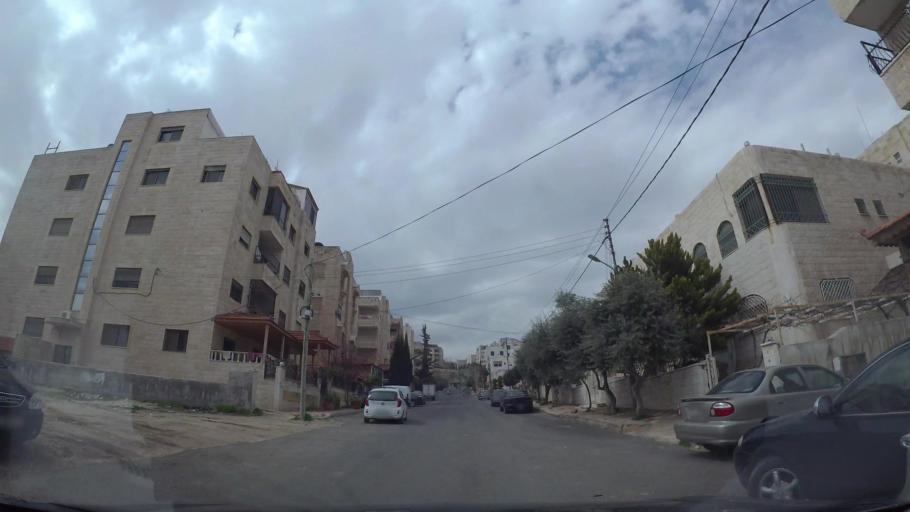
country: JO
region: Amman
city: Amman
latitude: 31.9910
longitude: 35.9261
